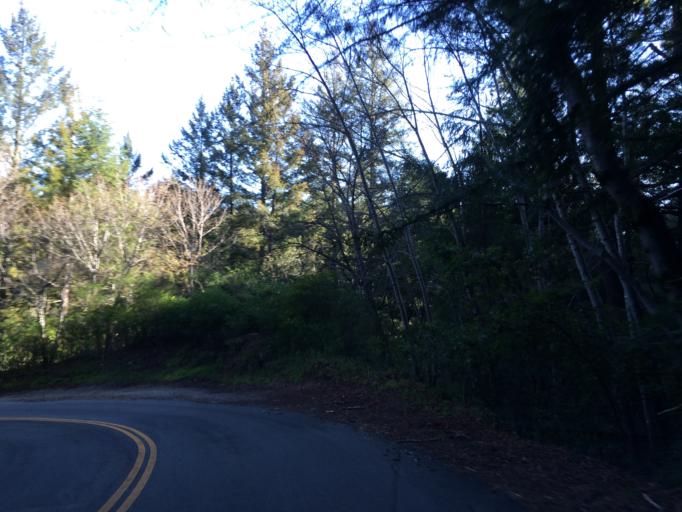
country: US
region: California
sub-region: Santa Cruz County
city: Boulder Creek
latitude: 37.1500
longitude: -122.1770
